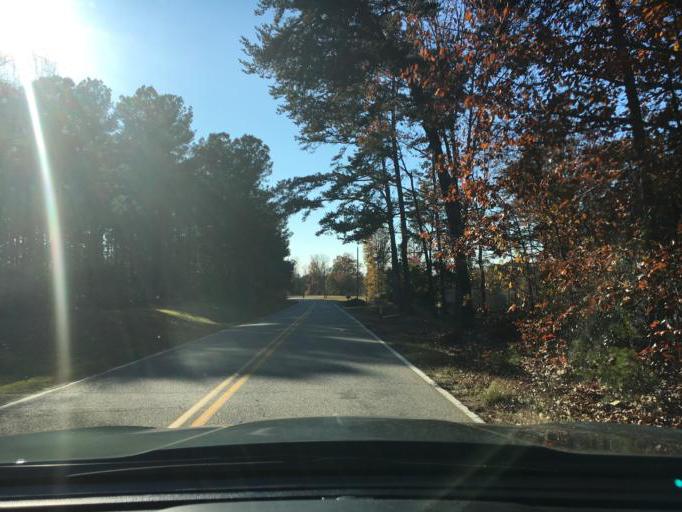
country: US
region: South Carolina
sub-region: Spartanburg County
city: Inman Mills
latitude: 35.0533
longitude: -82.1309
